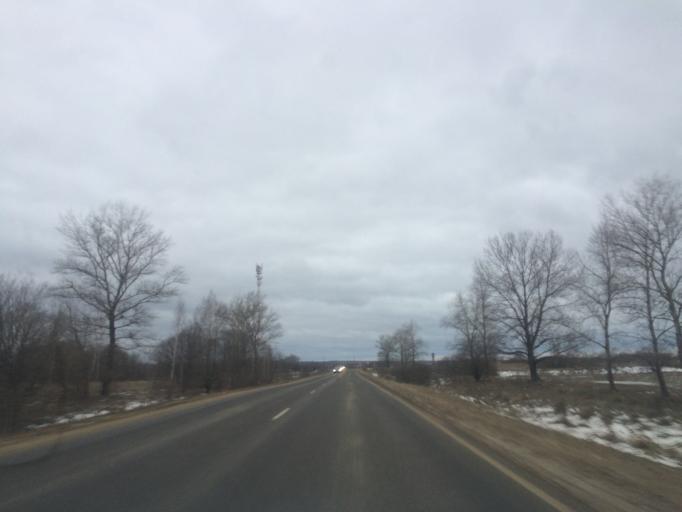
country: RU
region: Tula
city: Odoyev
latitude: 53.9949
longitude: 36.7441
